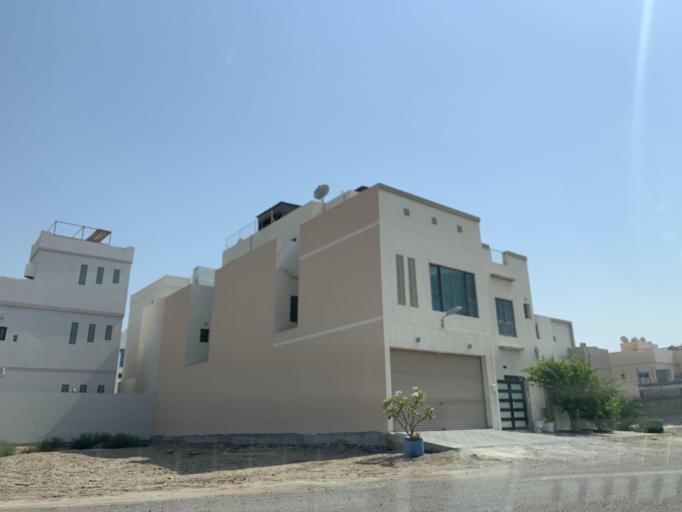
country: BH
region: Manama
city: Jidd Hafs
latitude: 26.2129
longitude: 50.5225
